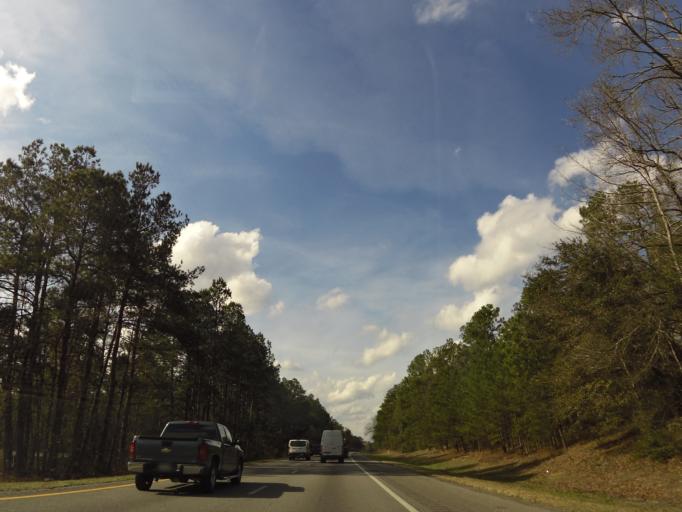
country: US
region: South Carolina
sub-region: Dorchester County
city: Ridgeville
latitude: 33.1532
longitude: -80.3433
